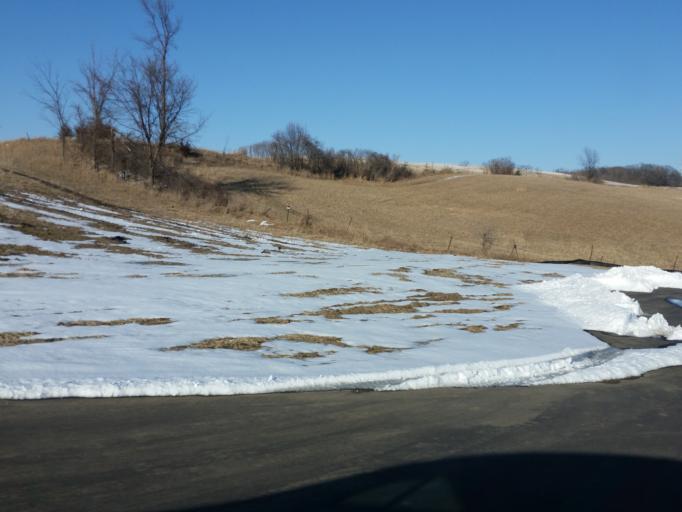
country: US
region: Minnesota
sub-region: Scott County
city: Elko New Market
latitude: 44.6275
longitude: -93.3595
